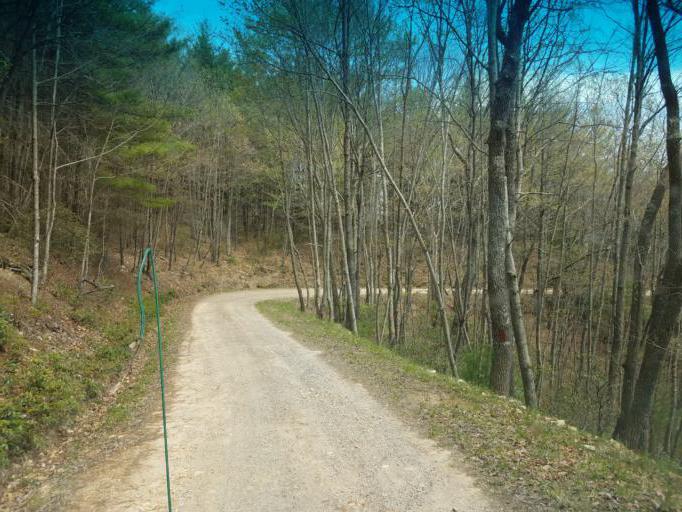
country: US
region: Virginia
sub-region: Smyth County
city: Marion
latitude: 36.7881
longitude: -81.4619
